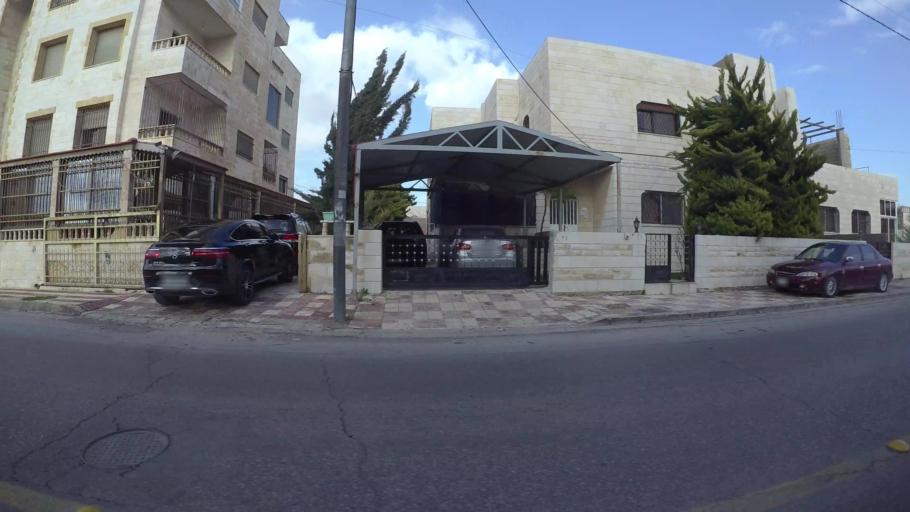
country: JO
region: Amman
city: Al Jubayhah
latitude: 31.9875
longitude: 35.8560
